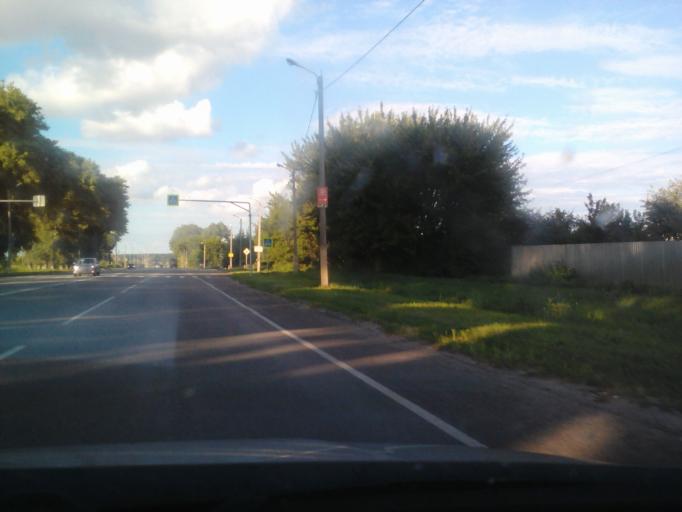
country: RU
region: Kursk
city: Kurchatov
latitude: 51.6620
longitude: 35.7226
